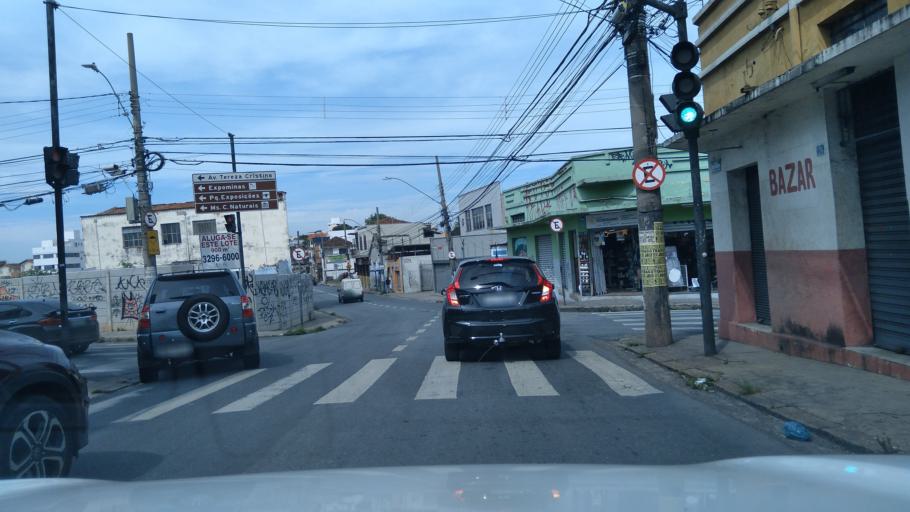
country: BR
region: Minas Gerais
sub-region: Belo Horizonte
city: Belo Horizonte
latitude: -19.9121
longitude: -43.9645
